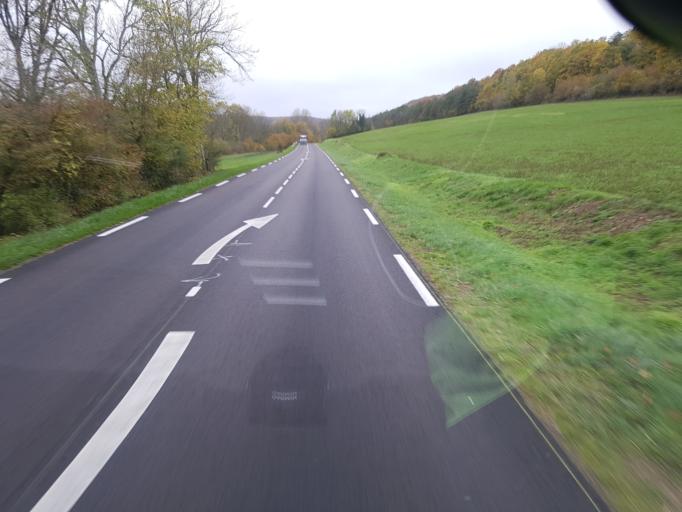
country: FR
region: Bourgogne
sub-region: Departement de la Cote-d'Or
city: Messigny-et-Vantoux
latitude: 47.5409
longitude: 4.9585
